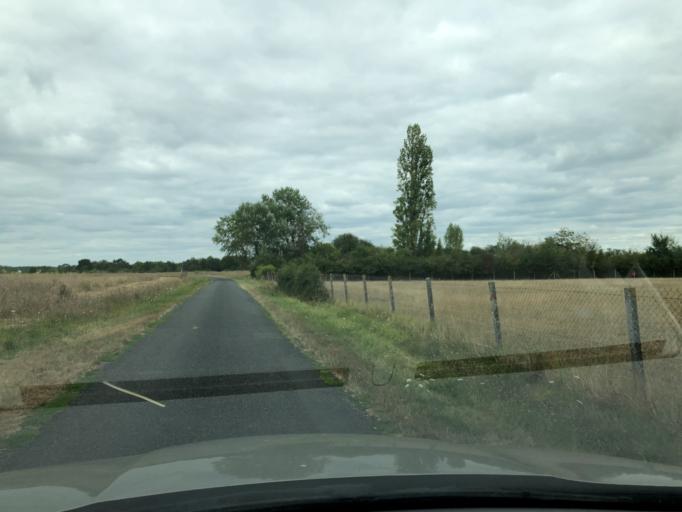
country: FR
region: Centre
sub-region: Departement d'Indre-et-Loire
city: Villandry
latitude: 47.3654
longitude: 0.4967
